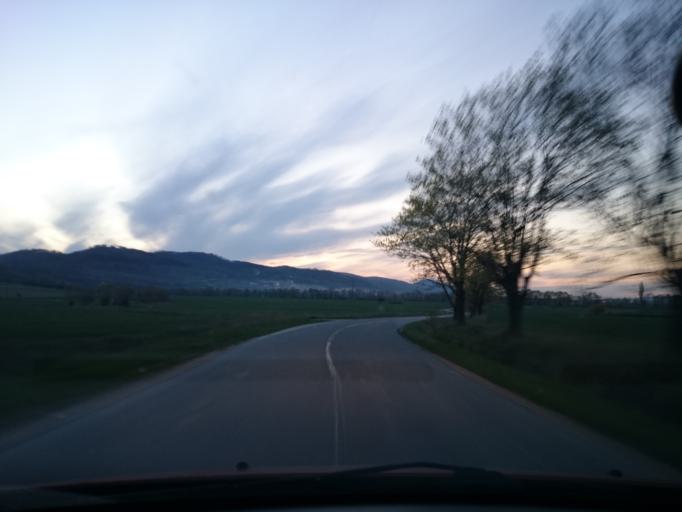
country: PL
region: Lower Silesian Voivodeship
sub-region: Powiat zabkowicki
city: Budzow
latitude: 50.5626
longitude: 16.6892
